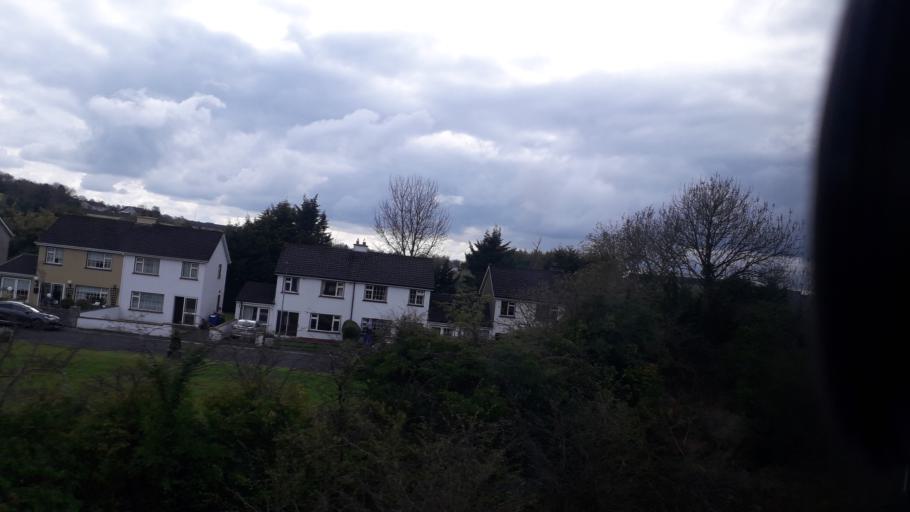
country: IE
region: Leinster
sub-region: An Longfort
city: Longford
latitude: 53.7265
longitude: -7.7827
